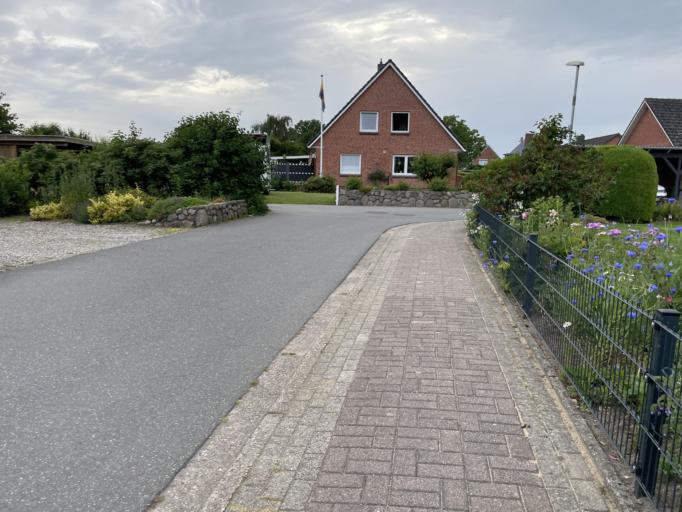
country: DE
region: Schleswig-Holstein
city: Mildstedt
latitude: 54.4623
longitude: 9.0920
